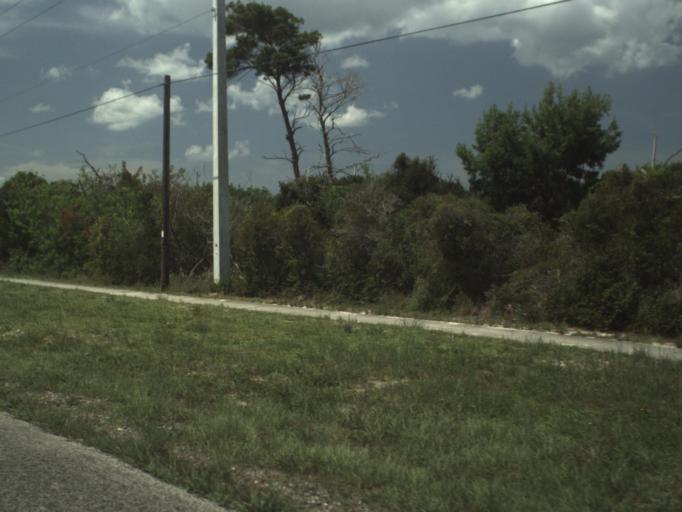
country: US
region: Florida
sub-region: Martin County
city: Hobe Sound
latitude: 27.0947
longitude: -80.1559
